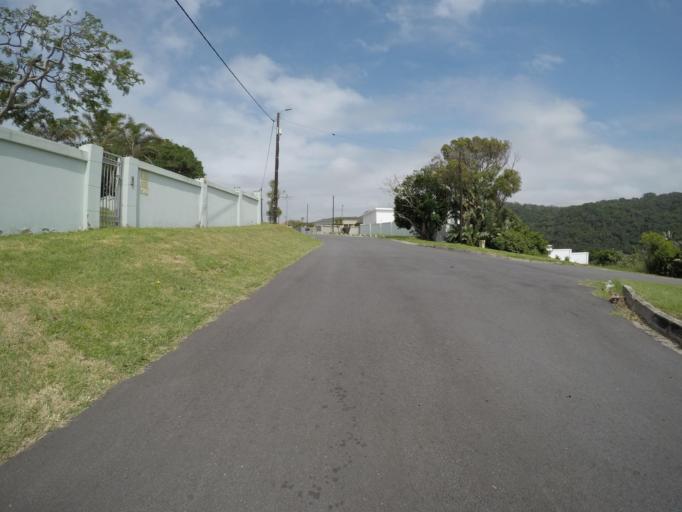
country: ZA
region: Eastern Cape
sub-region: Buffalo City Metropolitan Municipality
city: East London
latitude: -32.9337
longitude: 28.0280
